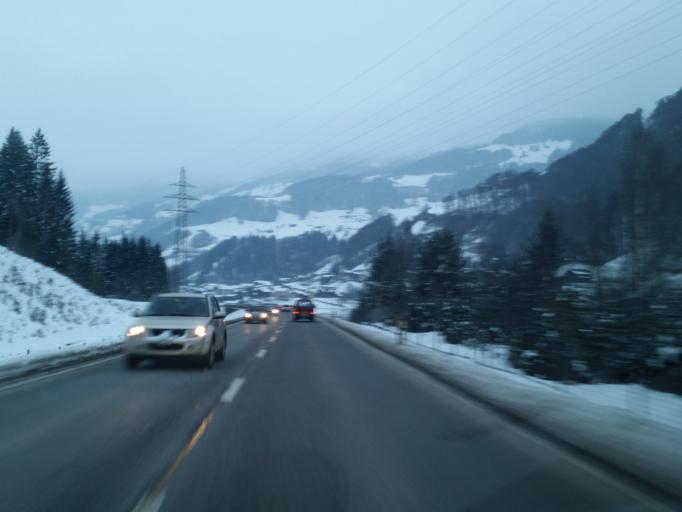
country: CH
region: Grisons
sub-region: Praettigau/Davos District
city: Schiers
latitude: 46.9602
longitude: 9.6992
